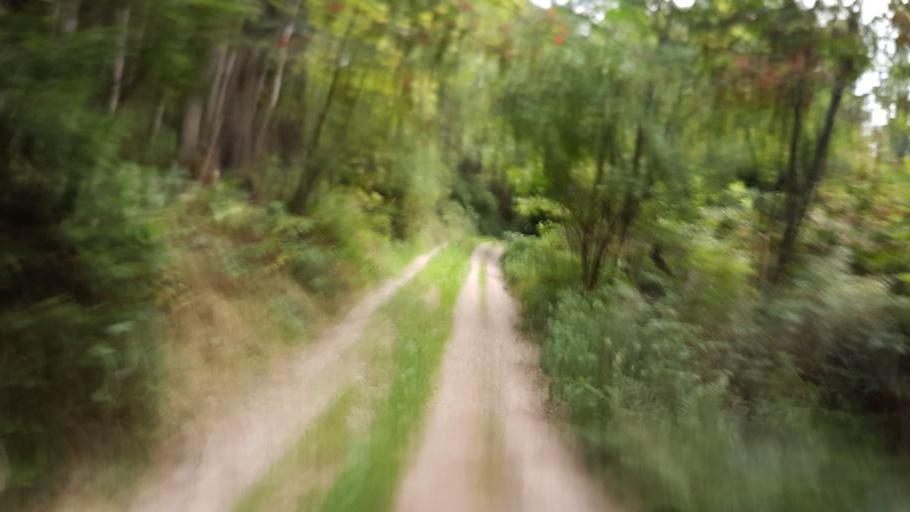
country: CH
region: Bern
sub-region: Bern-Mittelland District
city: Linden
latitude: 46.8615
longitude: 7.6912
